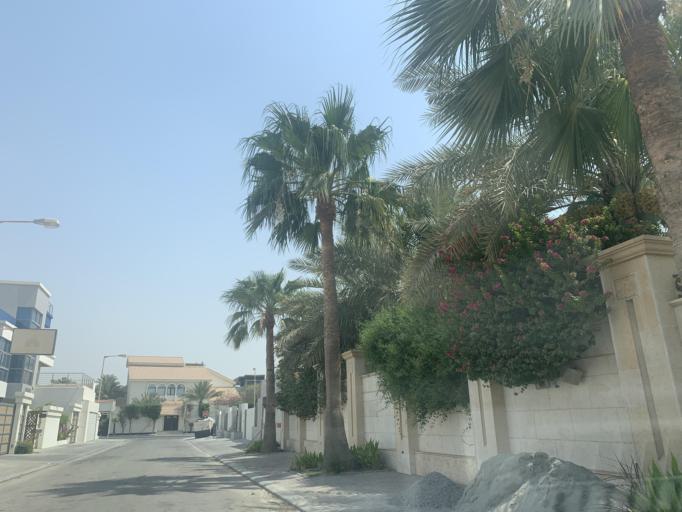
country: BH
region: Manama
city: Jidd Hafs
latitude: 26.1978
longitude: 50.4930
